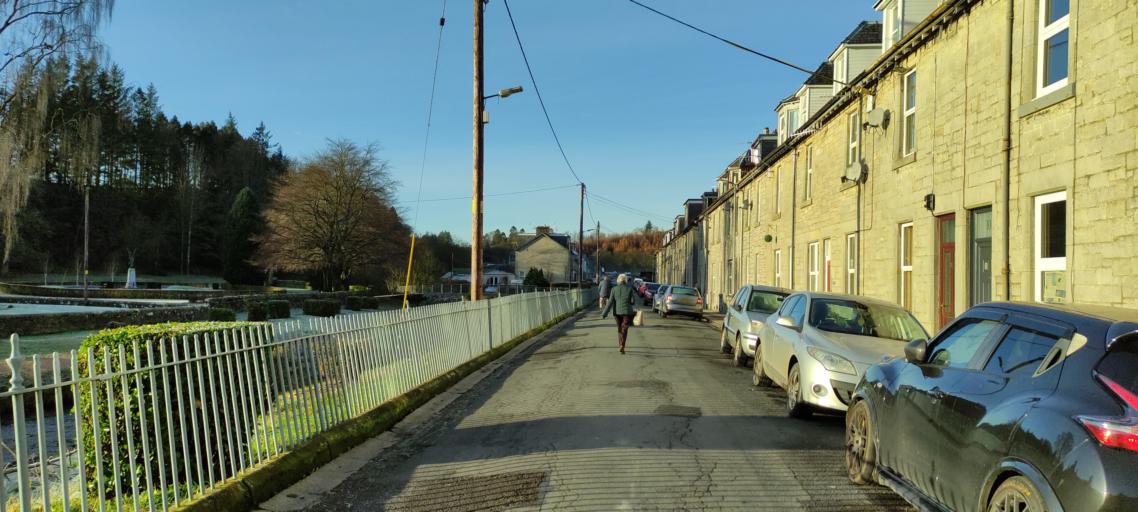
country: GB
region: Scotland
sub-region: Dumfries and Galloway
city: Langholm
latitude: 55.1511
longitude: -3.0028
